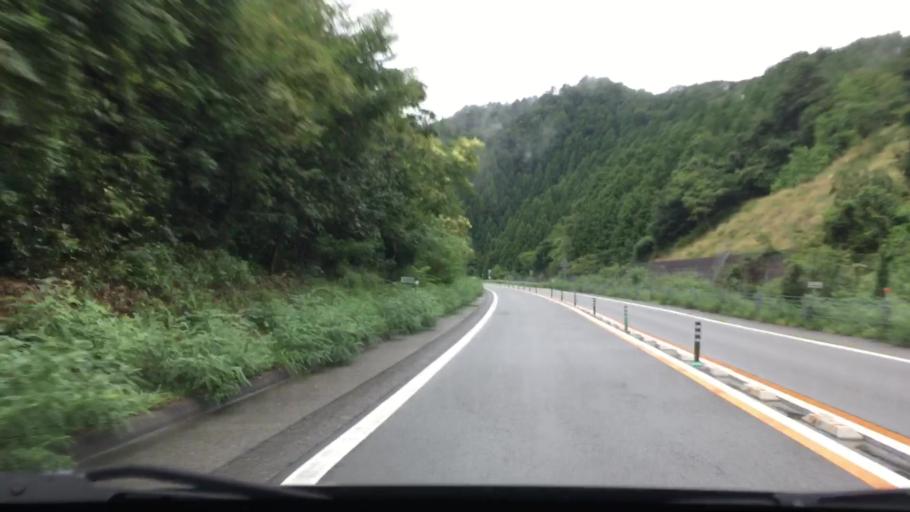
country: JP
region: Hyogo
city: Toyooka
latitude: 35.2583
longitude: 134.7952
